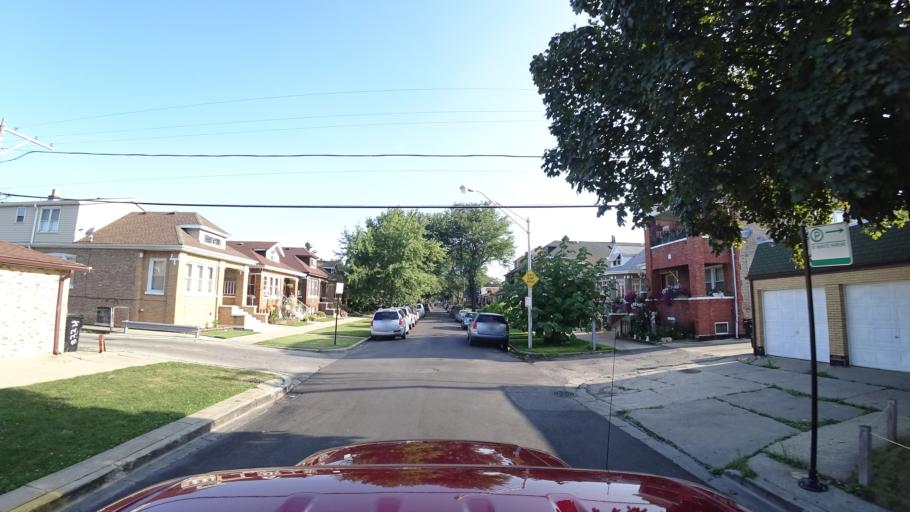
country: US
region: Illinois
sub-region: Cook County
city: Hometown
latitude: 41.7937
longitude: -87.7073
